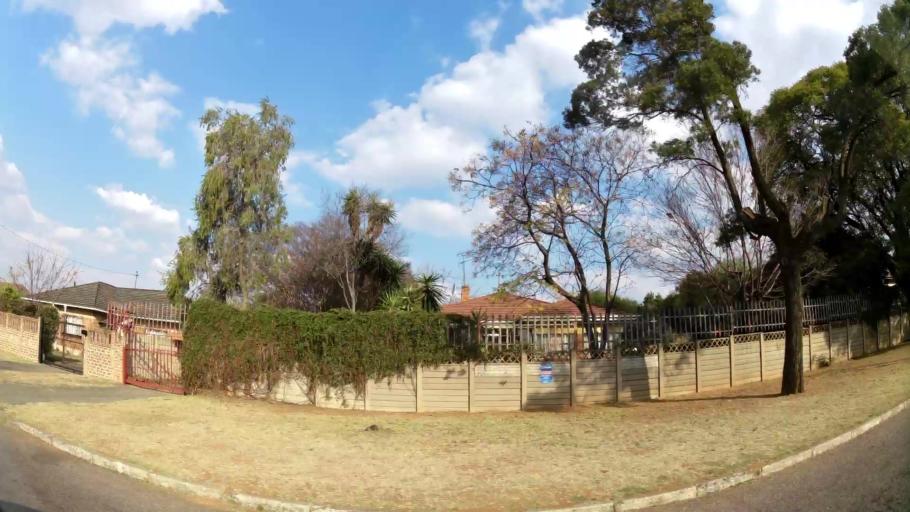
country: ZA
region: Gauteng
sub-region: Ekurhuleni Metropolitan Municipality
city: Germiston
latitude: -26.2305
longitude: 28.1795
